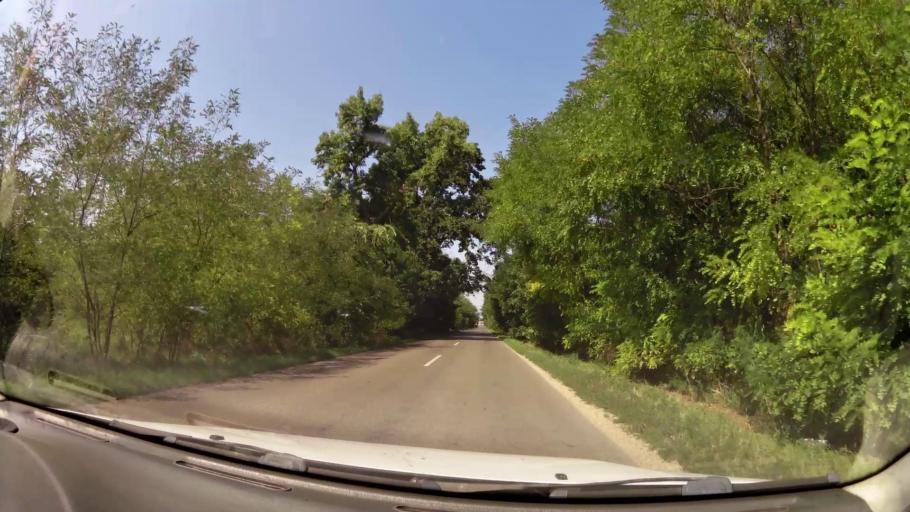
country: HU
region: Pest
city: Tapiosag
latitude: 47.3932
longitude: 19.6397
